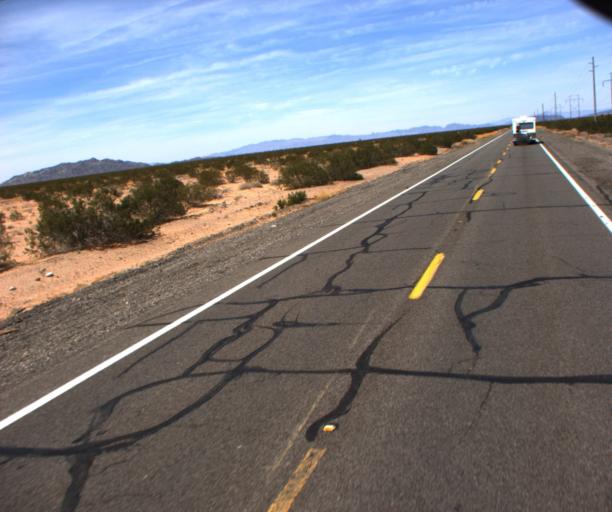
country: US
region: Arizona
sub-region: La Paz County
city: Parker
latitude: 33.9219
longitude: -114.2169
